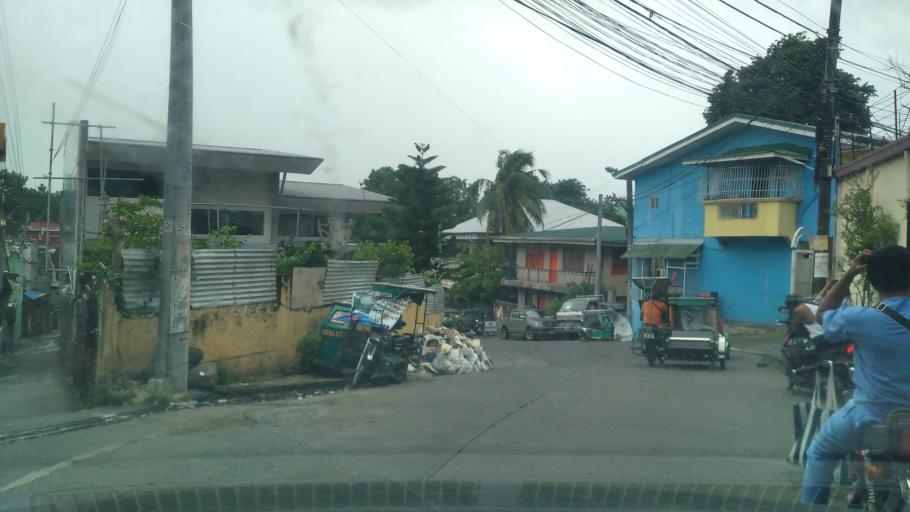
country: PH
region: Calabarzon
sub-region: Province of Quezon
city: Lucena
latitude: 13.9356
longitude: 121.6149
